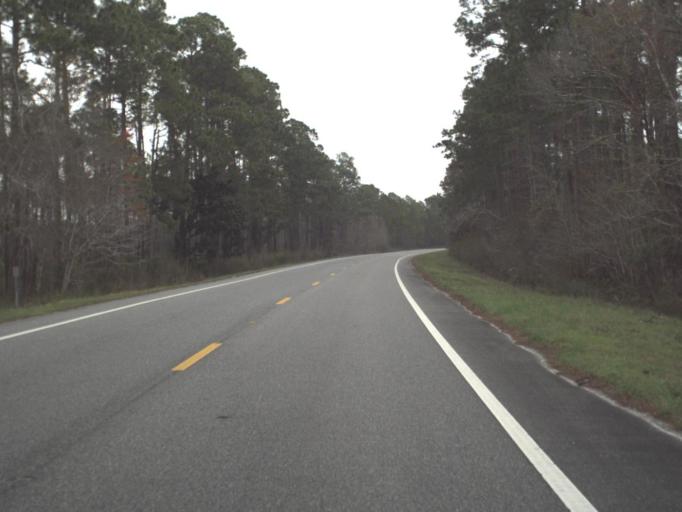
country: US
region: Florida
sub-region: Franklin County
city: Eastpoint
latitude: 29.8273
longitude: -84.8975
